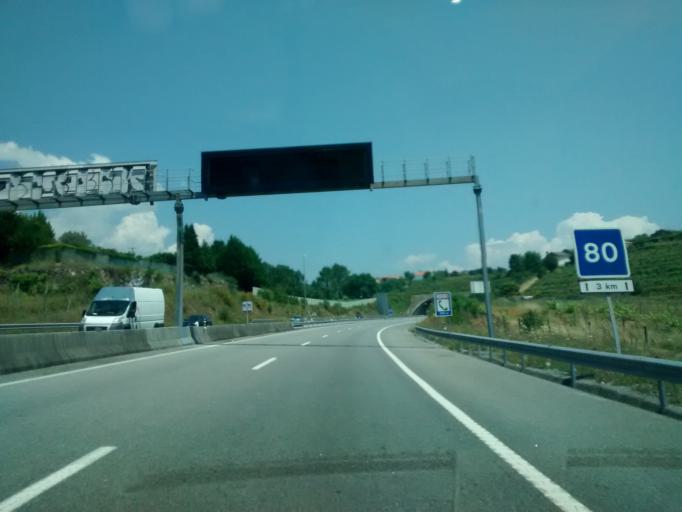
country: PT
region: Viana do Castelo
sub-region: Ponte de Lima
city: Ponte de Lima
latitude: 41.7870
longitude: -8.5859
